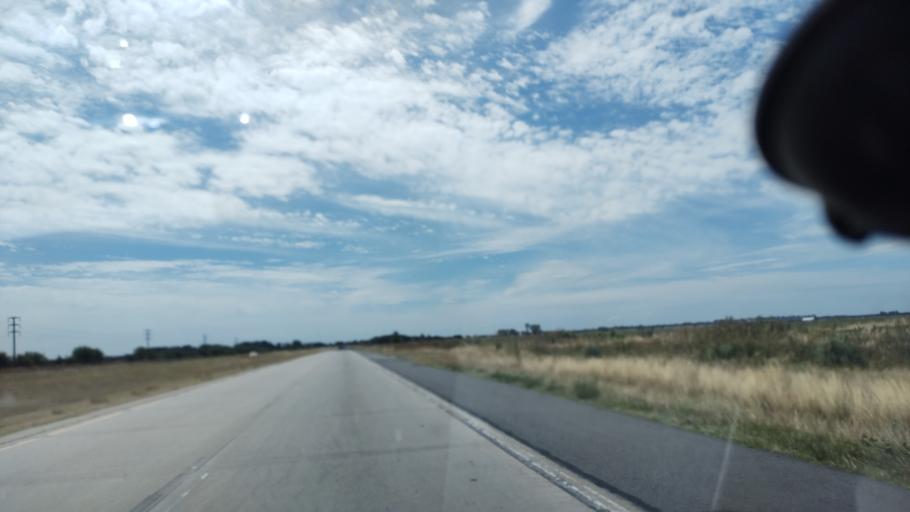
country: AR
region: Buenos Aires
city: Canuelas
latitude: -35.0684
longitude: -58.6997
